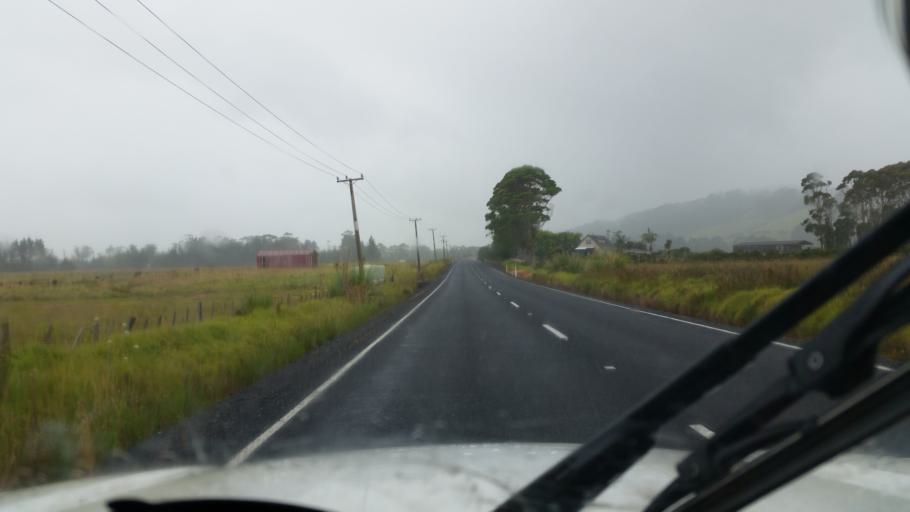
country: NZ
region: Northland
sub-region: Far North District
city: Ahipara
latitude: -35.1780
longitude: 173.1715
